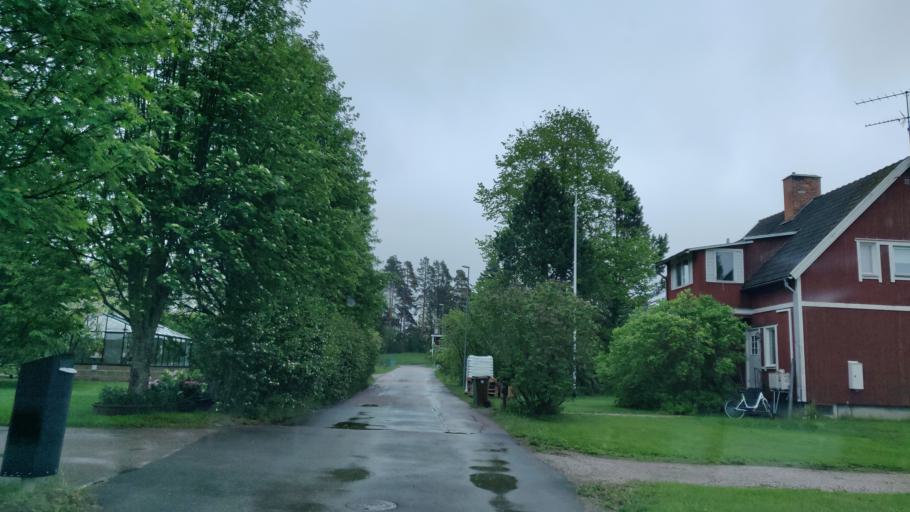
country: SE
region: Dalarna
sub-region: Avesta Kommun
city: Horndal
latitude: 60.3041
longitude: 16.4083
